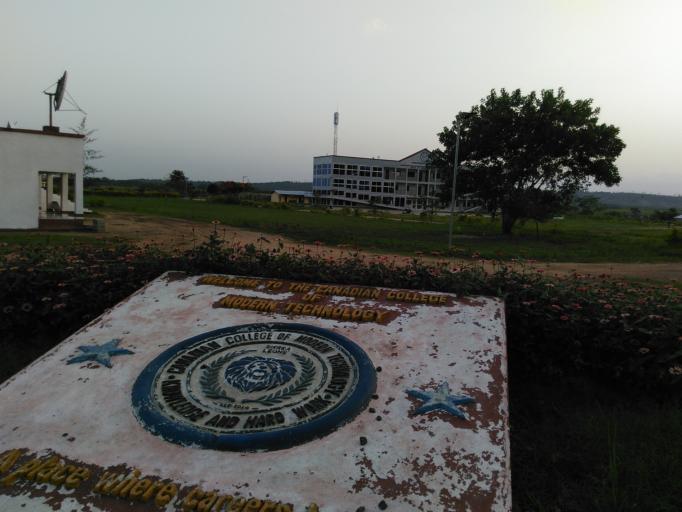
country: SL
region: Northern Province
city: Yonibana
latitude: 8.4689
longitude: -12.2418
